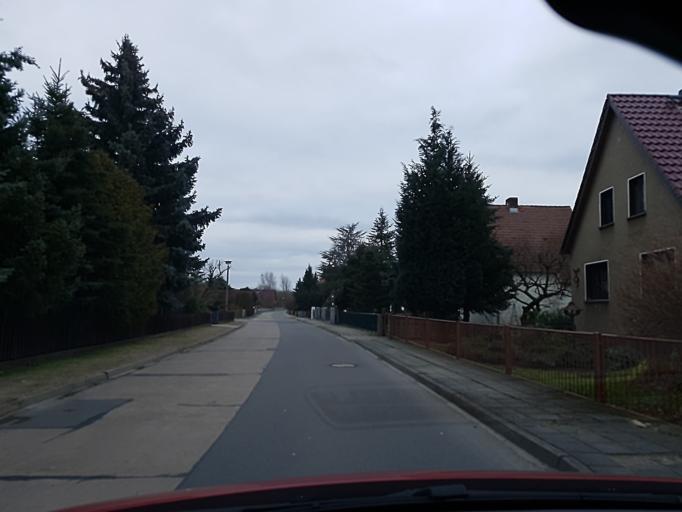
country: DE
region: Brandenburg
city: Elsterwerda
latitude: 51.4595
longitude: 13.5062
